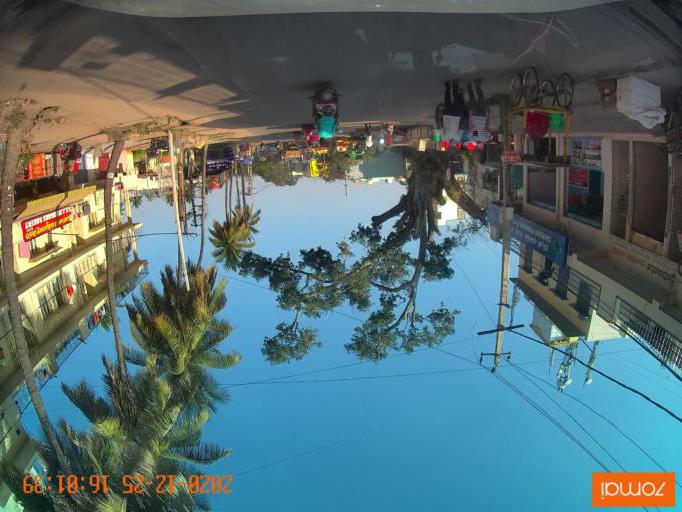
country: IN
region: Karnataka
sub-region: Bangalore Urban
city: Bangalore
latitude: 12.8797
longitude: 77.6245
